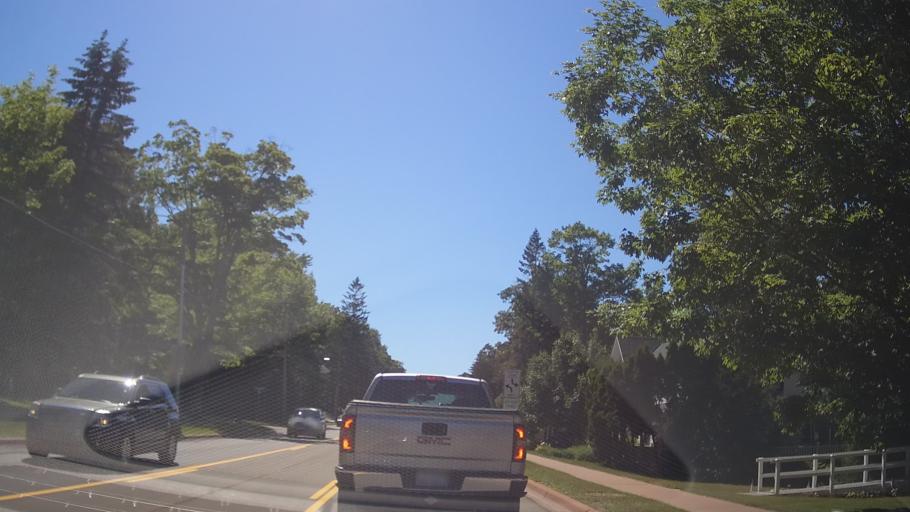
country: US
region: Michigan
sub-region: Emmet County
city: Petoskey
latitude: 45.3860
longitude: -84.9316
